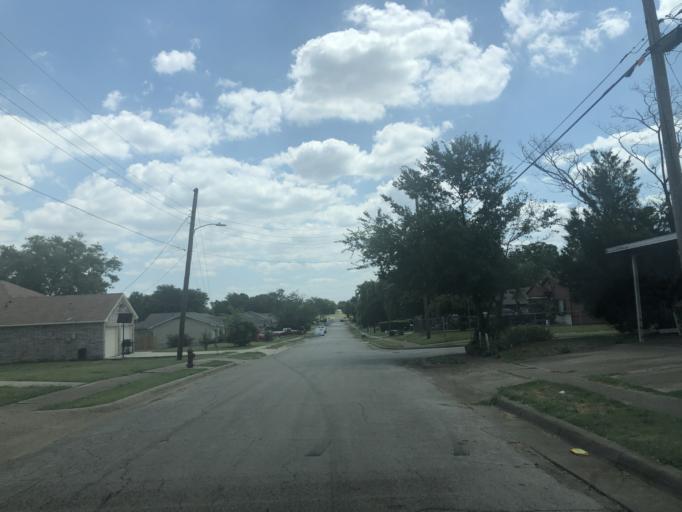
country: US
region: Texas
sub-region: Dallas County
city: Grand Prairie
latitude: 32.7361
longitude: -97.0314
